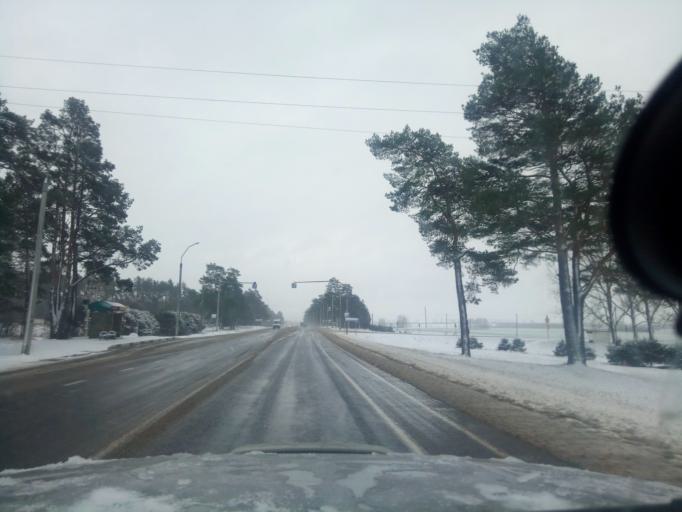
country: BY
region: Minsk
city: Nyasvizh
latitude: 53.2473
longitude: 26.6244
